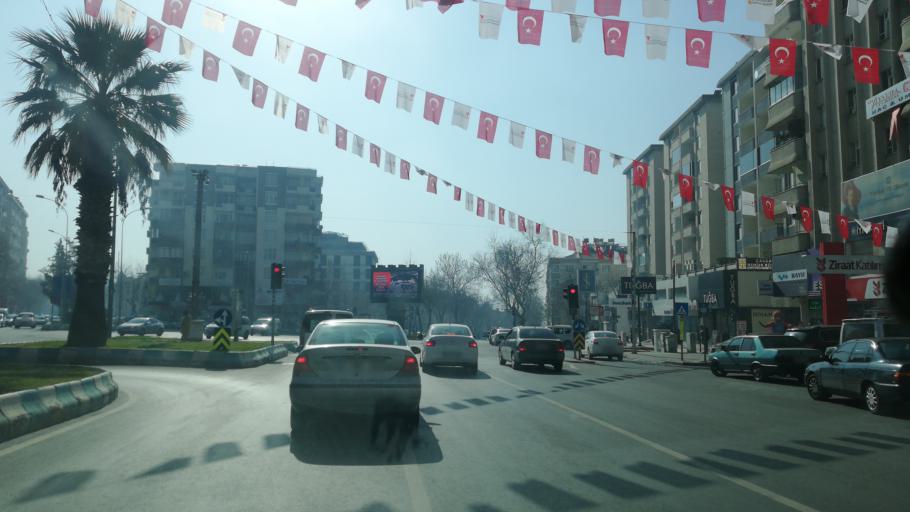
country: TR
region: Kahramanmaras
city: Kahramanmaras
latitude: 37.5752
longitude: 36.9327
